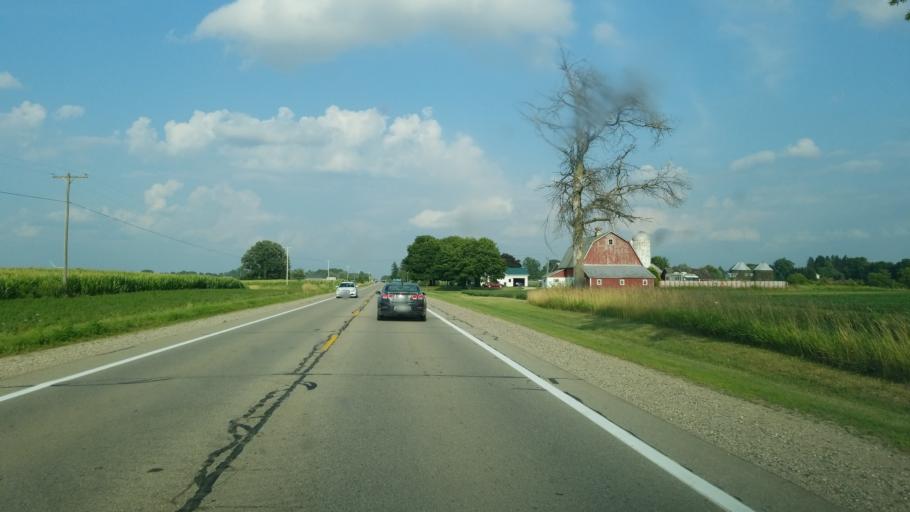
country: US
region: Michigan
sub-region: Gratiot County
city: Alma
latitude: 43.4081
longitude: -84.6958
